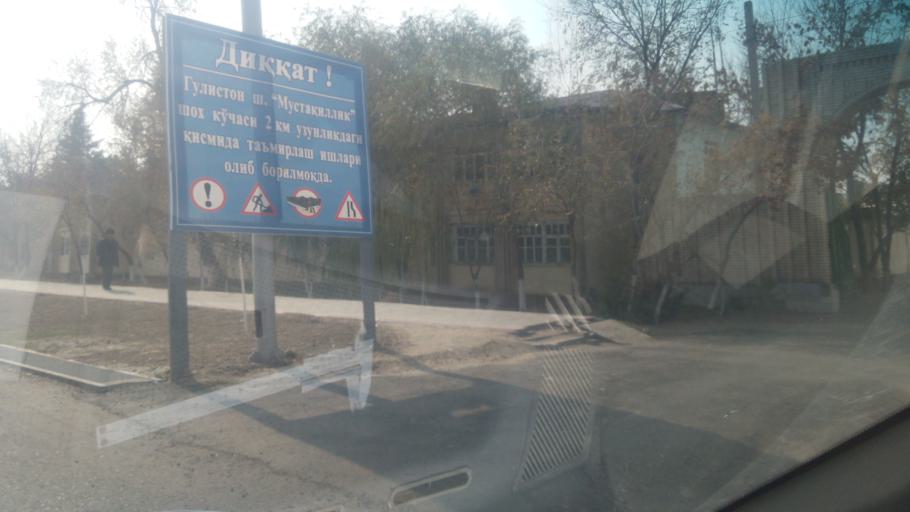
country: UZ
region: Sirdaryo
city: Guliston
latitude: 40.5099
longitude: 68.7729
